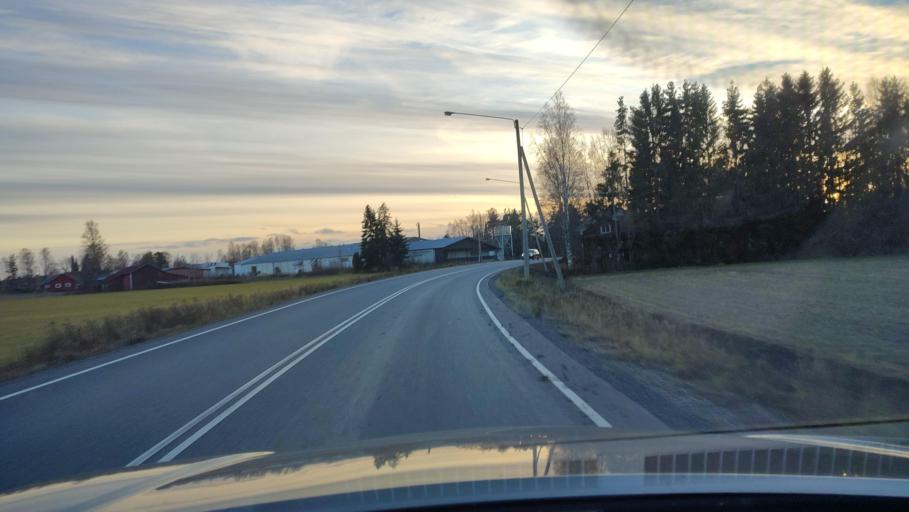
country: FI
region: Ostrobothnia
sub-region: Sydosterbotten
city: Kristinestad
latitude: 62.2643
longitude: 21.5409
